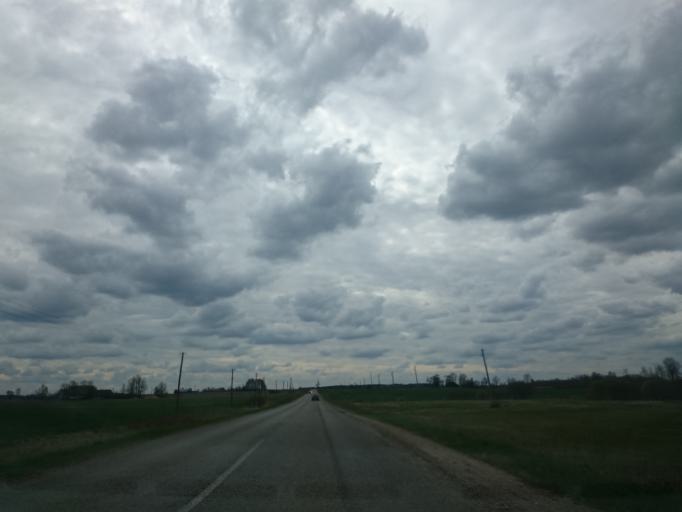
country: LV
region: Talsu Rajons
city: Sabile
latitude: 56.9581
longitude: 22.6131
